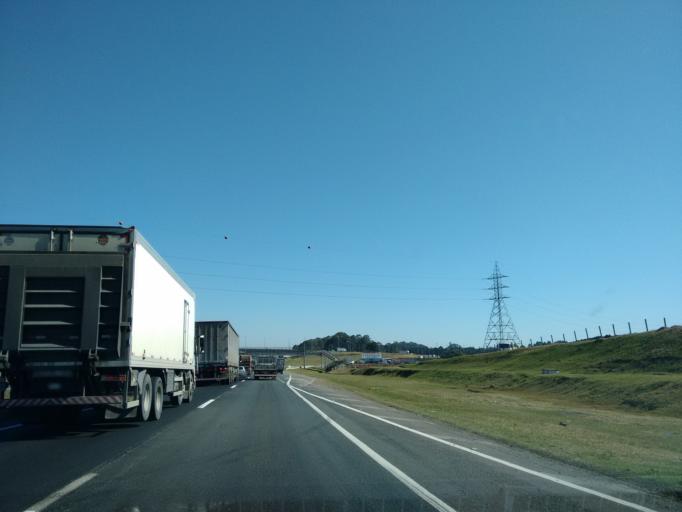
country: BR
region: Parana
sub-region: Sao Jose Dos Pinhais
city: Sao Jose dos Pinhais
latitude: -25.5454
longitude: -49.2972
